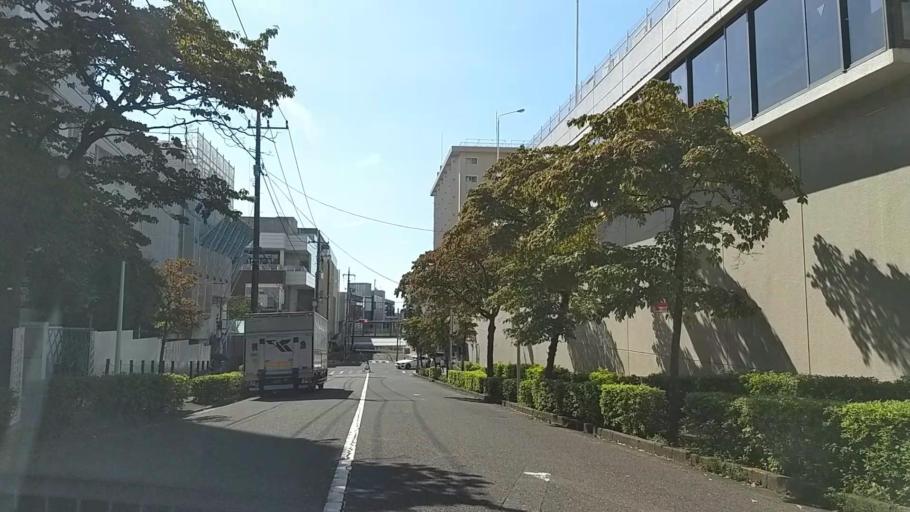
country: JP
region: Tokyo
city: Chofugaoka
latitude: 35.5785
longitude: 139.5570
